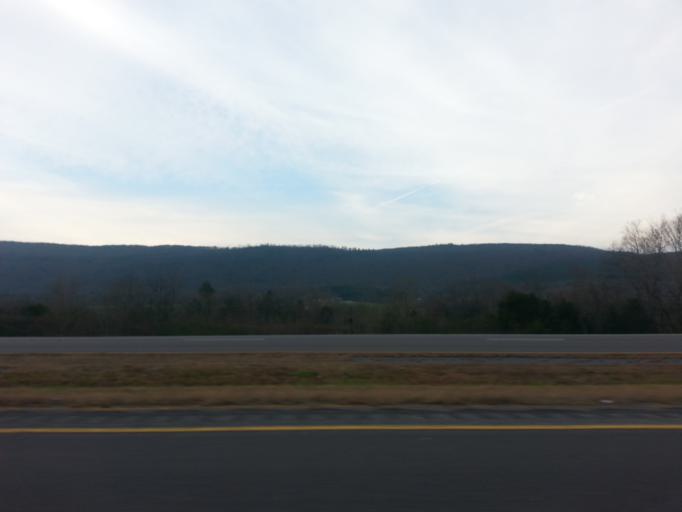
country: US
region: Tennessee
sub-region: Rhea County
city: Spring City
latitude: 35.5998
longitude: -84.9237
